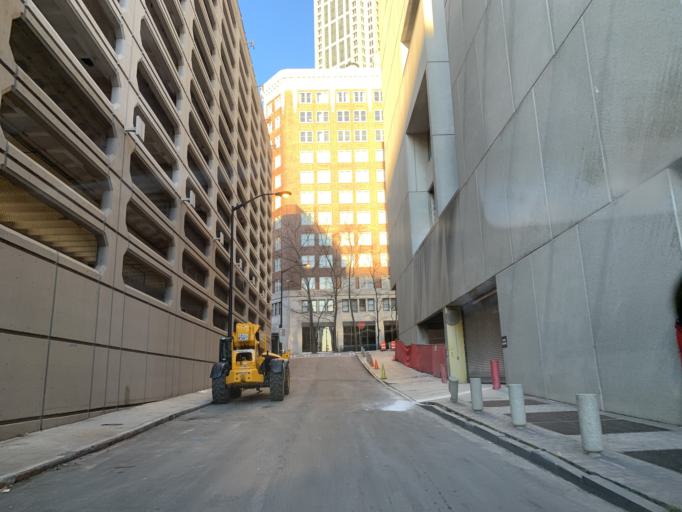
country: US
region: Georgia
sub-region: Fulton County
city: Atlanta
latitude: 33.7578
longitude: -84.3889
